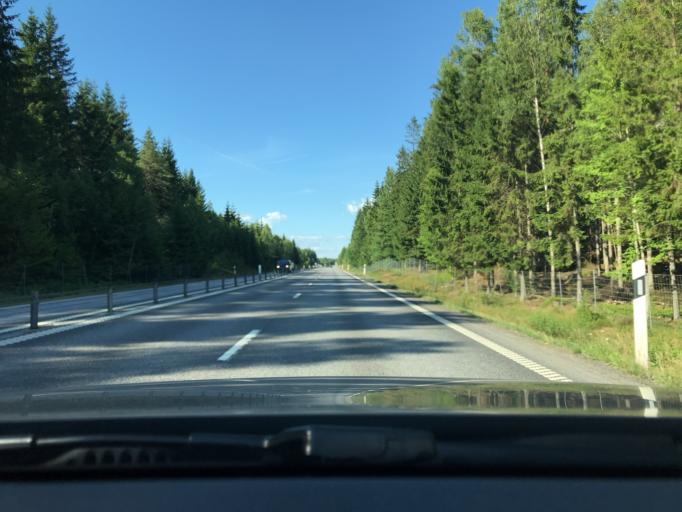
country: SE
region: Skane
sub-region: Osby Kommun
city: Osby
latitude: 56.4226
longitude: 14.0545
